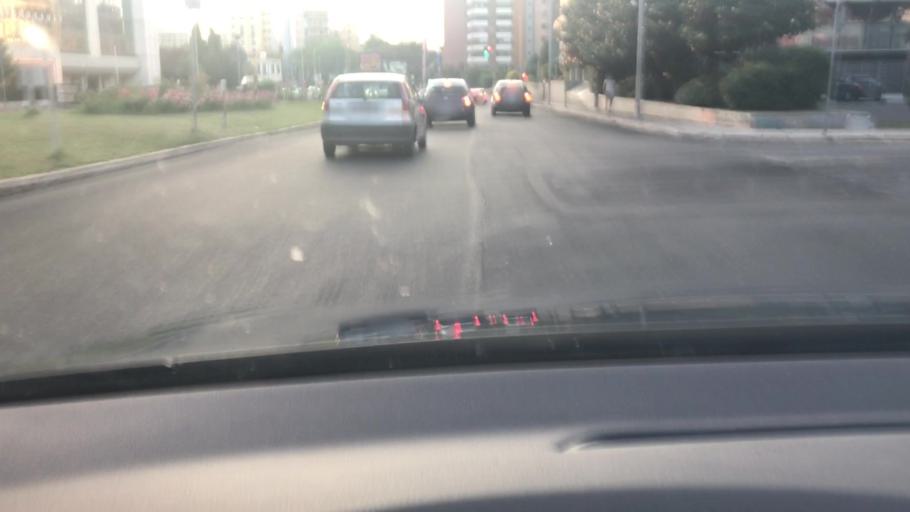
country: IT
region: Latium
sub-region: Citta metropolitana di Roma Capitale
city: Rome
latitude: 41.9301
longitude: 12.5622
